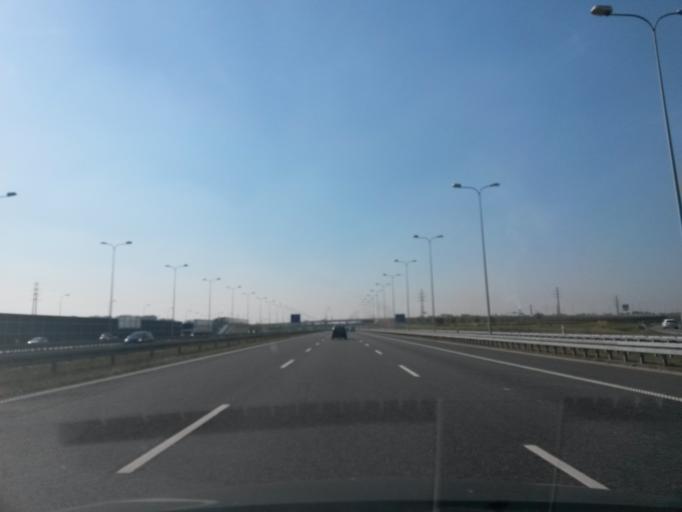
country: PL
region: Silesian Voivodeship
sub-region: Powiat gliwicki
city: Przyszowice
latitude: 50.2642
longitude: 18.7333
